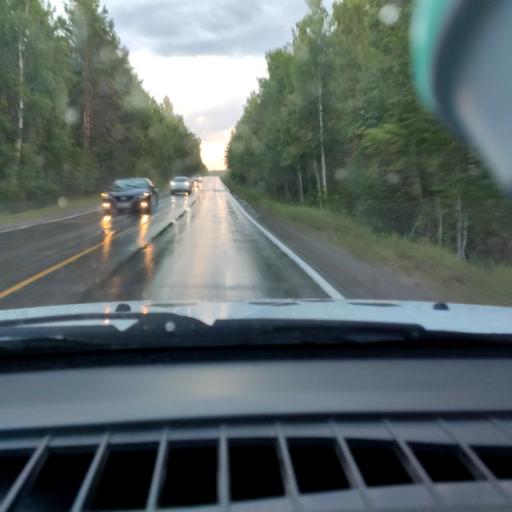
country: RU
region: Chelyabinsk
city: Ozersk
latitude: 55.8161
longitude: 60.6397
